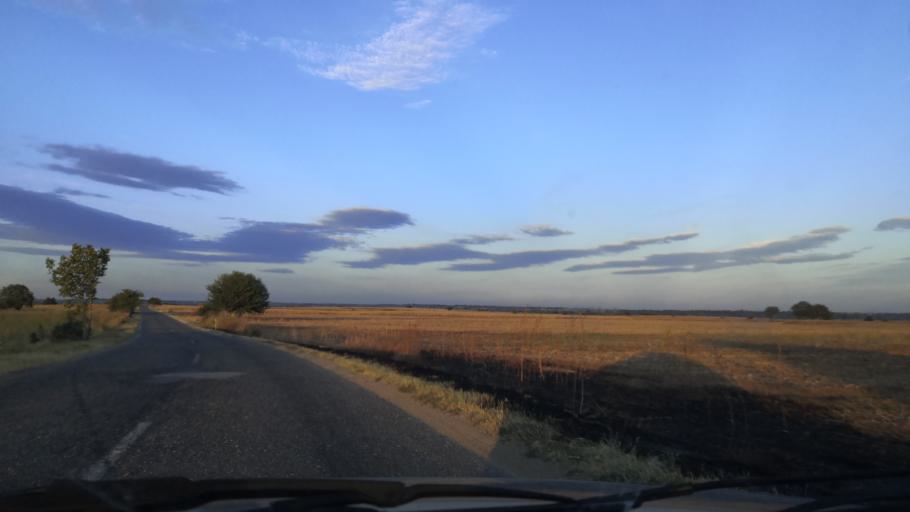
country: RO
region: Mehedinti
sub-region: Comuna Gruia
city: Izvoarele
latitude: 44.2540
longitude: 22.6274
